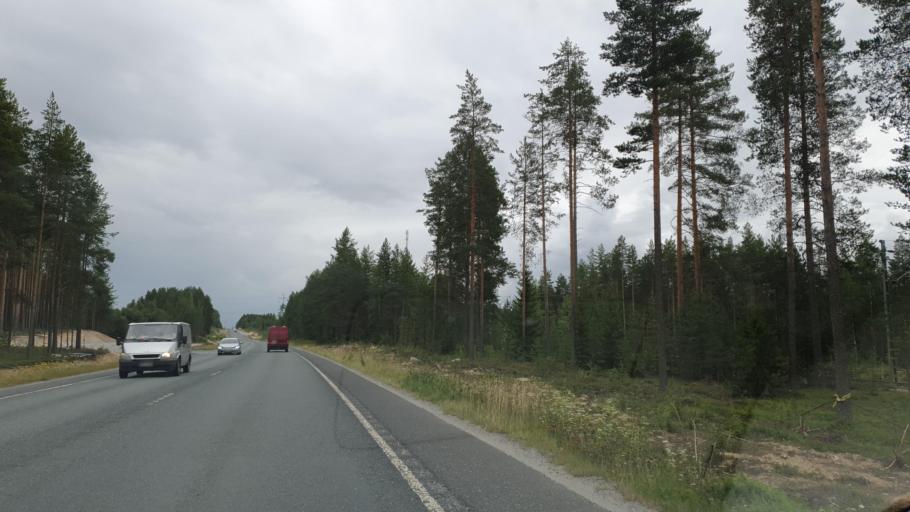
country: FI
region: Northern Savo
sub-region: Ylae-Savo
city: Lapinlahti
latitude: 63.2777
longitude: 27.4577
